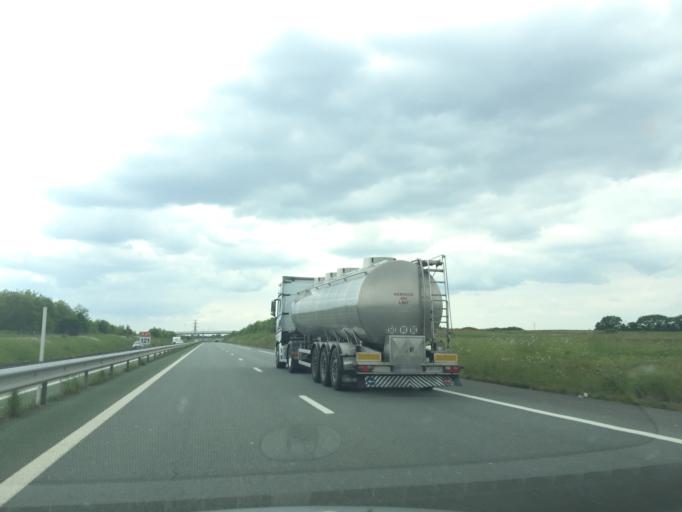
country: FR
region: Poitou-Charentes
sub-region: Departement des Deux-Sevres
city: Villiers-en-Plaine
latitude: 46.4142
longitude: -0.5680
